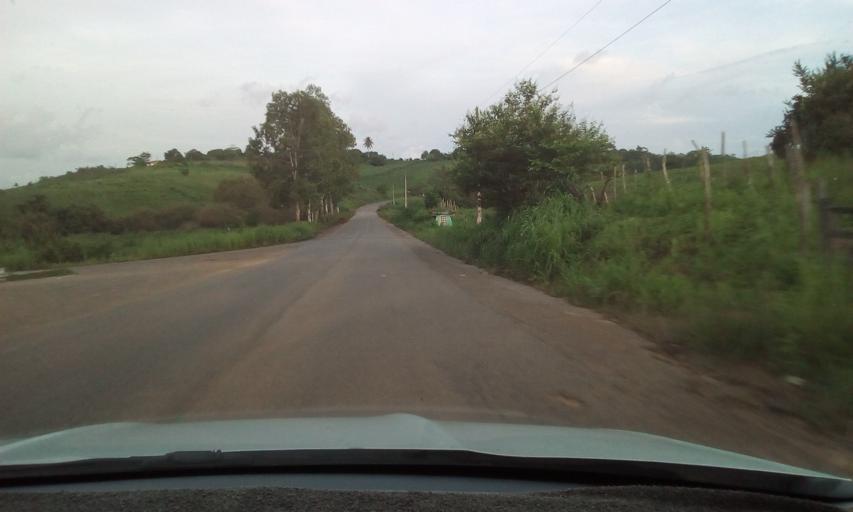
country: BR
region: Pernambuco
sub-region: Condado
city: Condado
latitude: -7.5982
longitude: -35.2160
